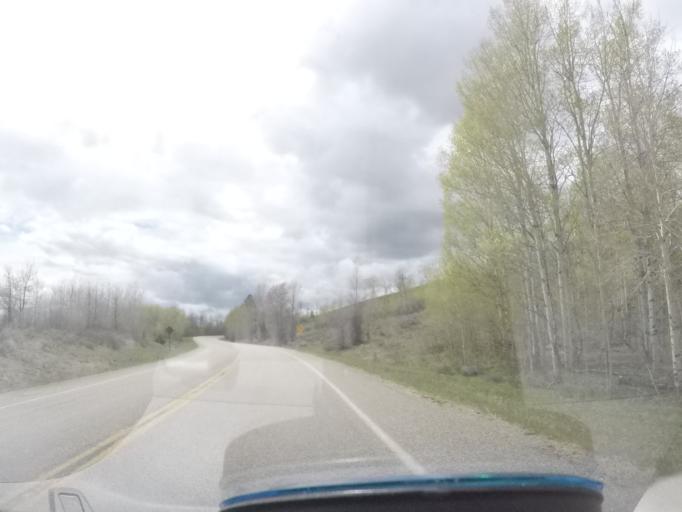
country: US
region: Wyoming
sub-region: Teton County
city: Jackson
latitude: 43.8390
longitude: -110.4770
